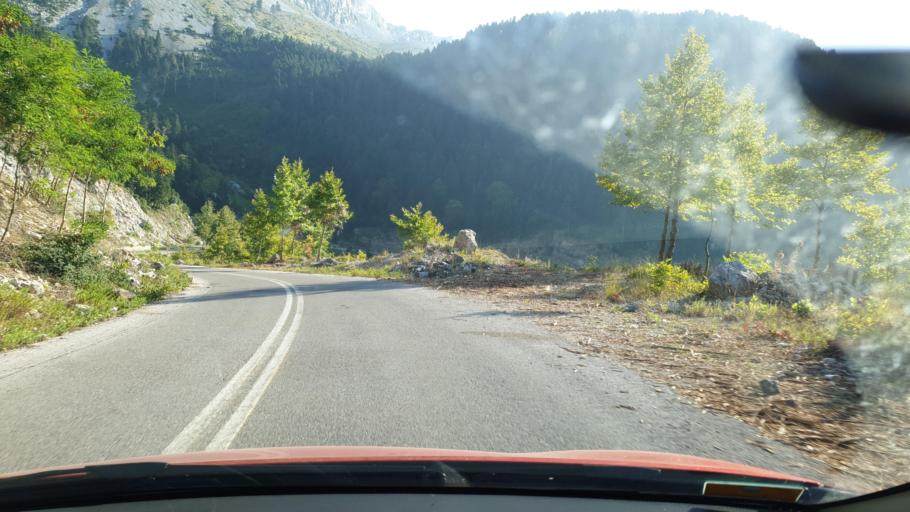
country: GR
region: Central Greece
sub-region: Nomos Evvoias
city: Yimnon
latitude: 38.5970
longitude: 23.9065
